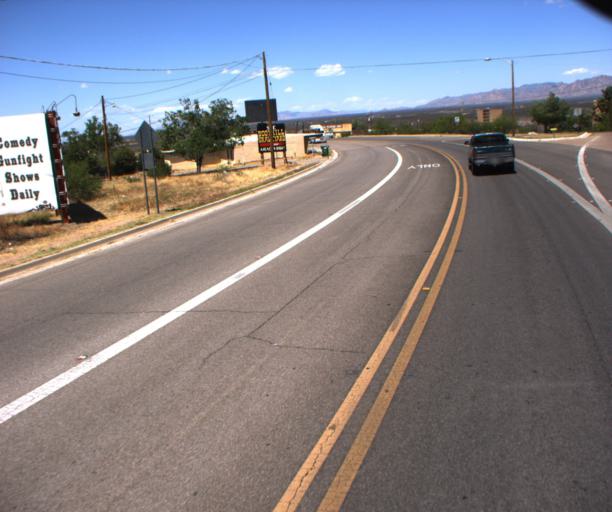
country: US
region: Arizona
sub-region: Cochise County
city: Tombstone
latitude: 31.7173
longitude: -110.0700
